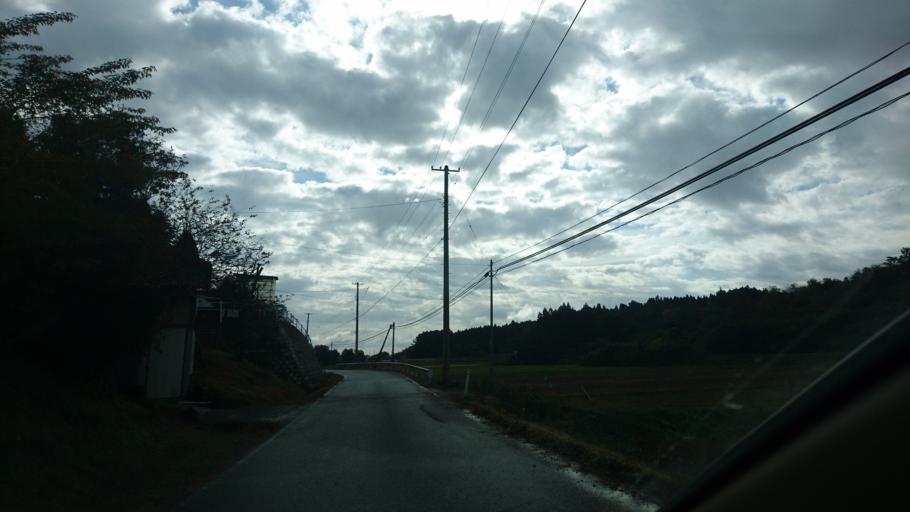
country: JP
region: Iwate
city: Ichinoseki
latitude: 38.7883
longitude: 141.0021
